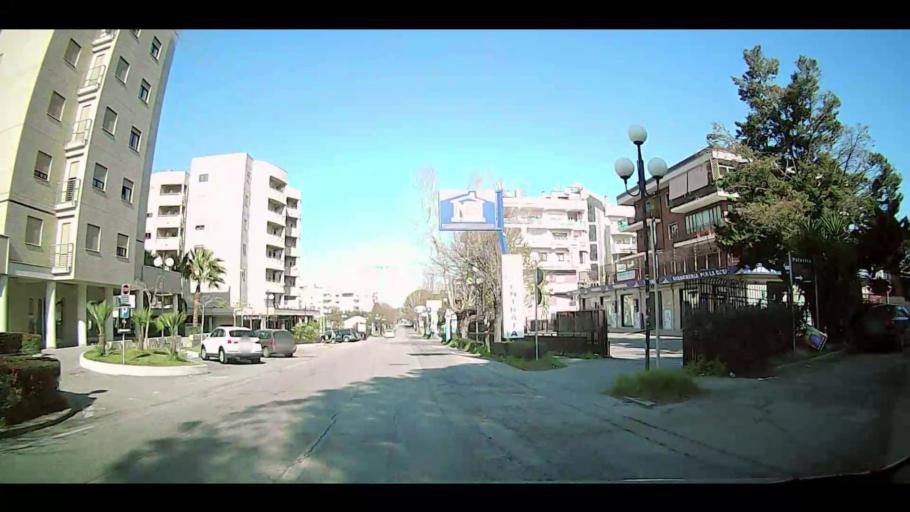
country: IT
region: Calabria
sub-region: Provincia di Cosenza
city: Quattromiglia
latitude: 39.3432
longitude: 16.2433
